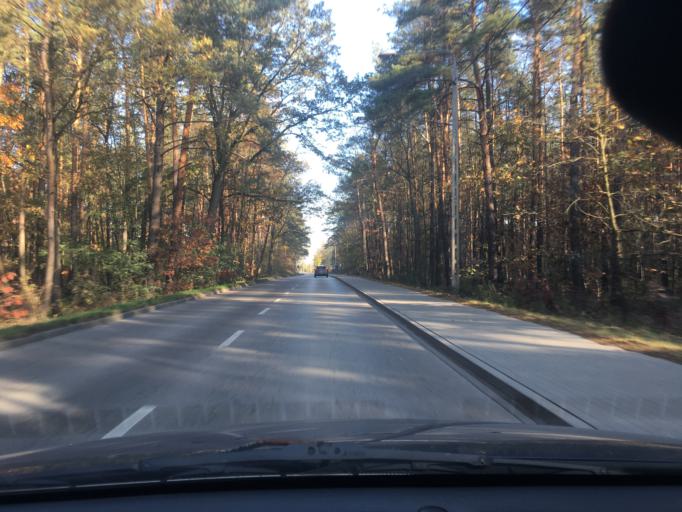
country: PL
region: Masovian Voivodeship
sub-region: Powiat piaseczynski
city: Lesznowola
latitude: 52.0798
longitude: 20.9381
